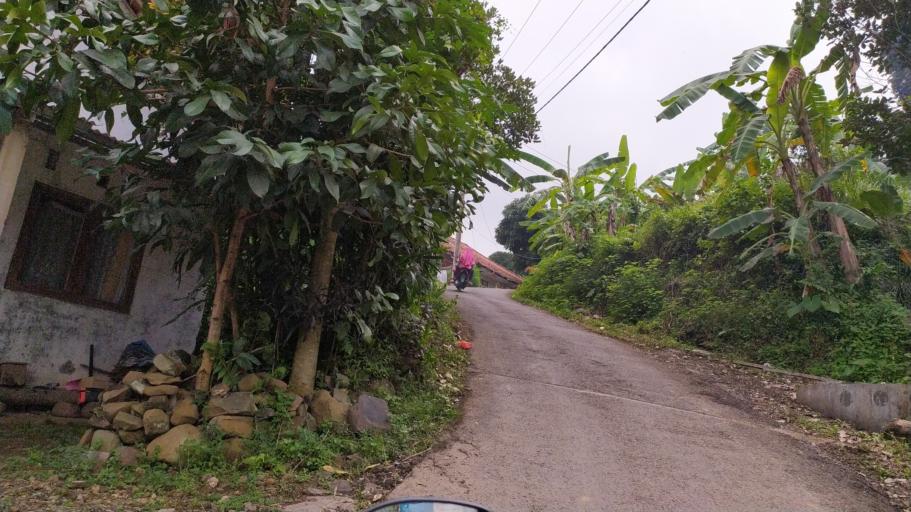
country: ID
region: West Java
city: Ciampea
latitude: -6.6257
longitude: 106.7136
